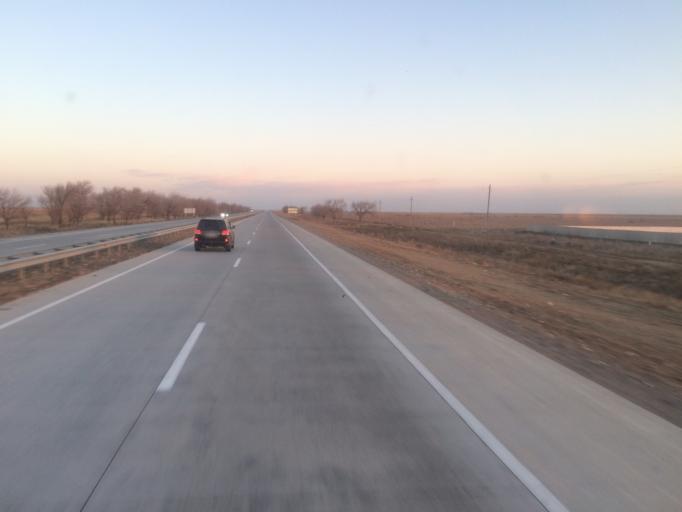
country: KZ
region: Ongtustik Qazaqstan
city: Bayaldyr
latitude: 43.0585
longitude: 68.6870
